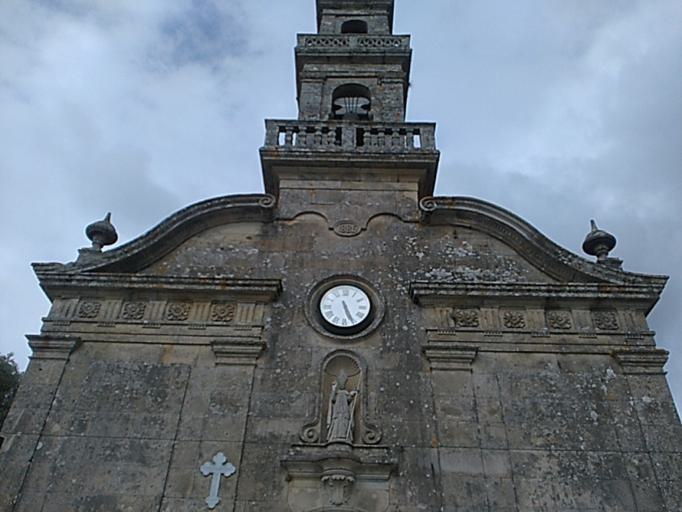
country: ES
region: Galicia
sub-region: Provincia de Pontevedra
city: Cangas
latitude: 42.2791
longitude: -8.8161
